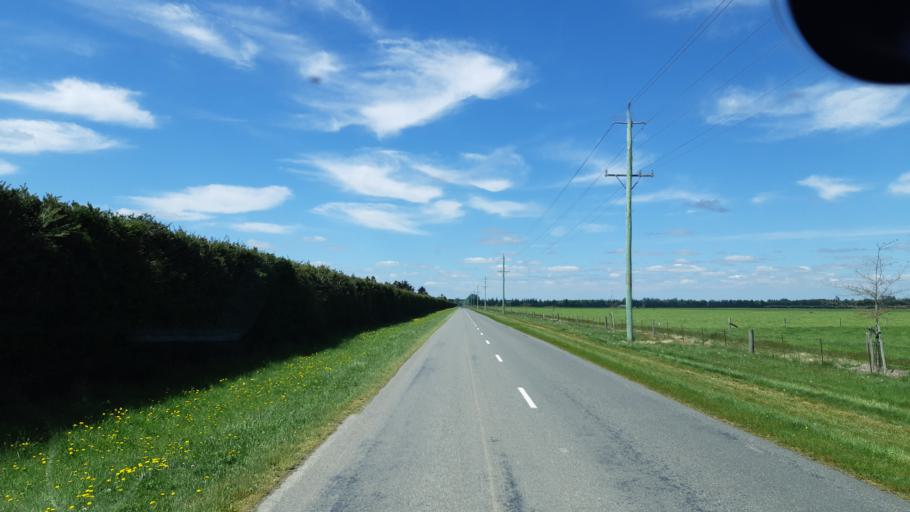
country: NZ
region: Canterbury
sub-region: Ashburton District
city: Methven
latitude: -43.7252
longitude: 171.4904
